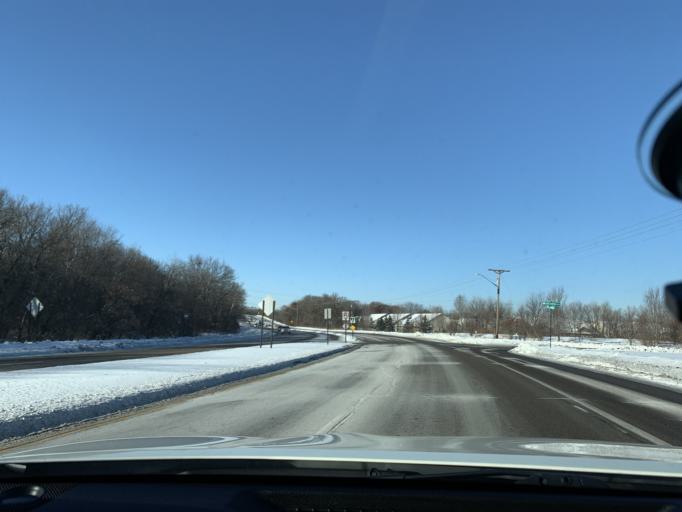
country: US
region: Minnesota
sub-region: Anoka County
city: Coon Rapids
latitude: 45.1461
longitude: -93.2837
